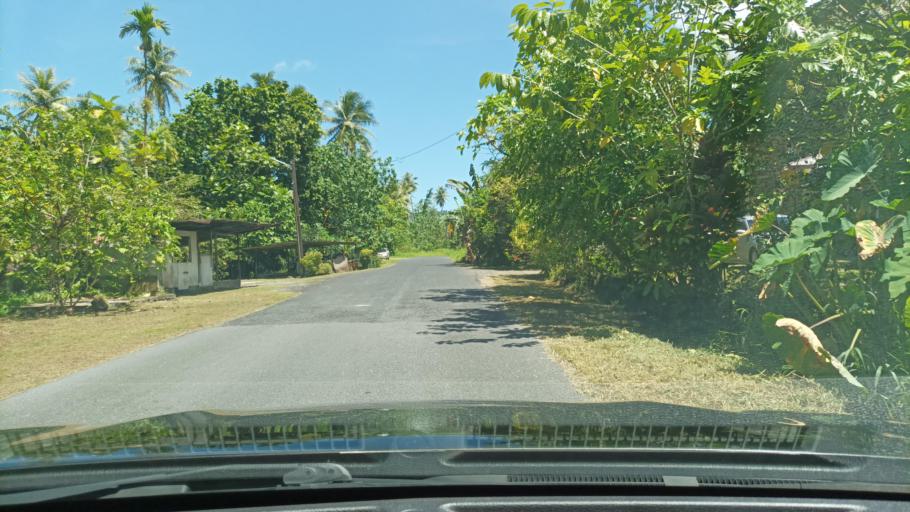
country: FM
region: Pohnpei
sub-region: Kolonia Municipality
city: Kolonia
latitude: 6.9472
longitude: 158.2746
